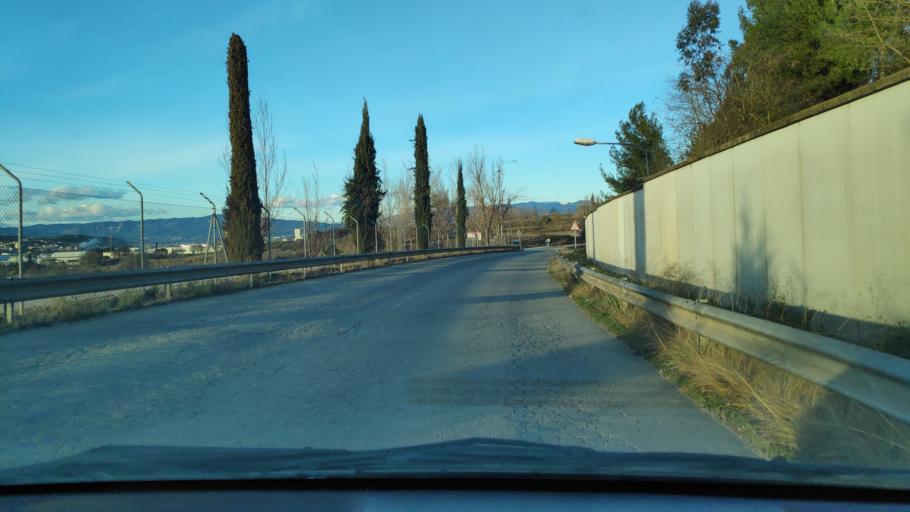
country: ES
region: Catalonia
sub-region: Provincia de Barcelona
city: Montmelo
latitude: 41.5662
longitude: 2.2514
